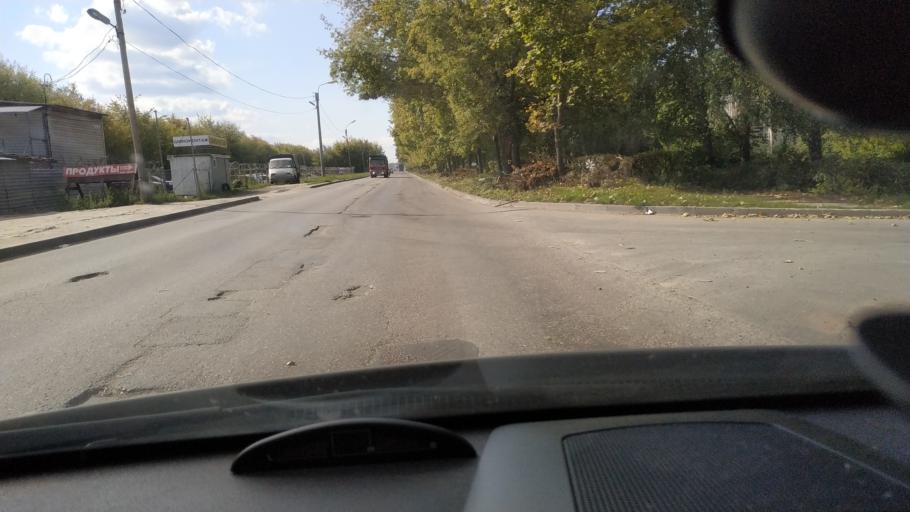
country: RU
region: Rjazan
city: Ryazan'
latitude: 54.6501
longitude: 39.6523
